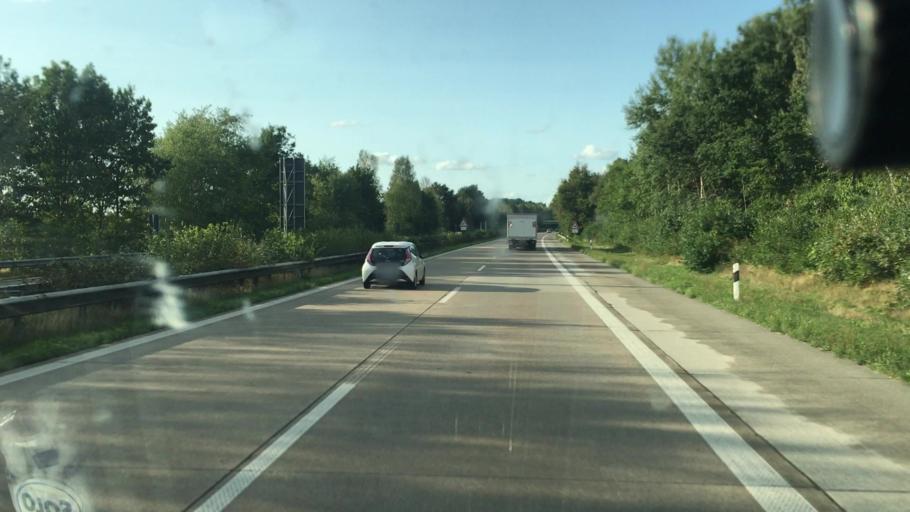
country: DE
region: Lower Saxony
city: Wiefelstede
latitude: 53.2835
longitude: 8.1528
